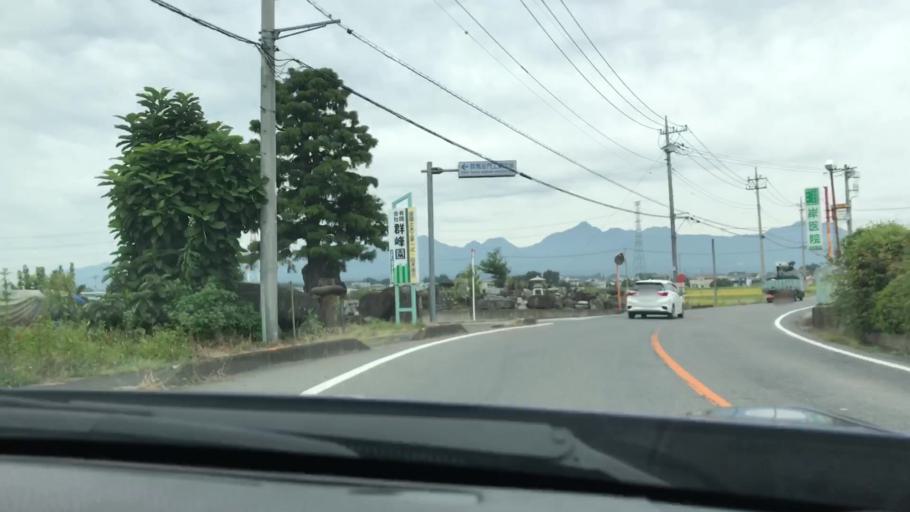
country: JP
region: Gunma
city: Kanekomachi
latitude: 36.3994
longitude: 138.9906
